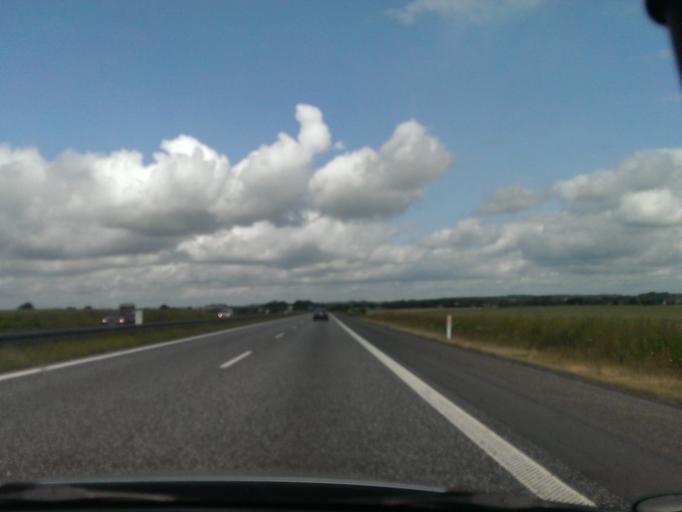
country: DK
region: Central Jutland
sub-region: Randers Kommune
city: Spentrup
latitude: 56.5321
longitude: 9.9290
